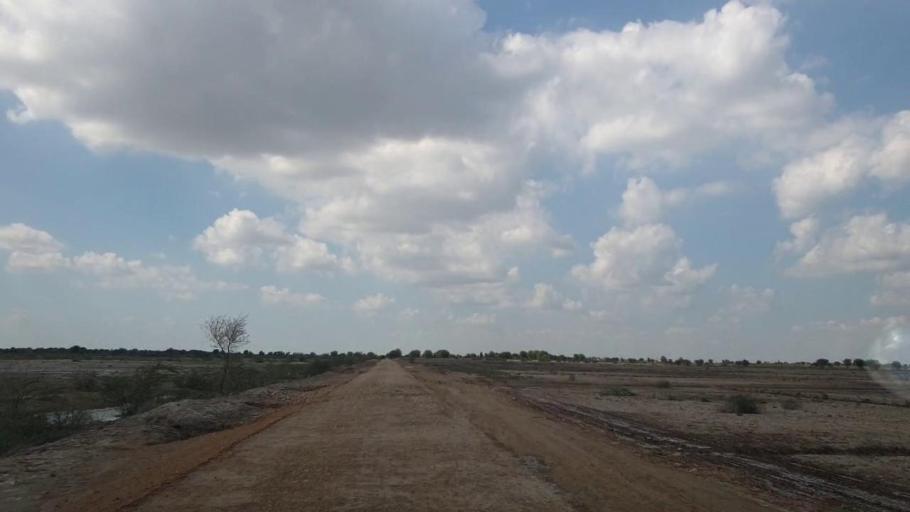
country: PK
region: Sindh
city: Pithoro
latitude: 25.6006
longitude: 69.3590
